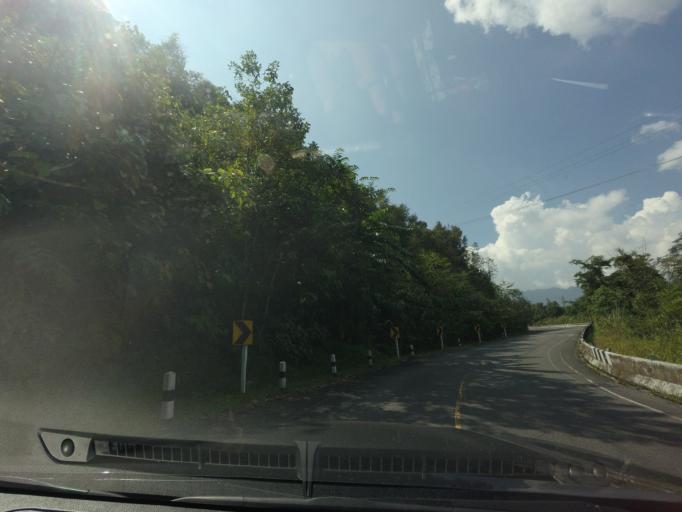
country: TH
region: Nan
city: Bo Kluea
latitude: 19.0691
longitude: 101.1232
